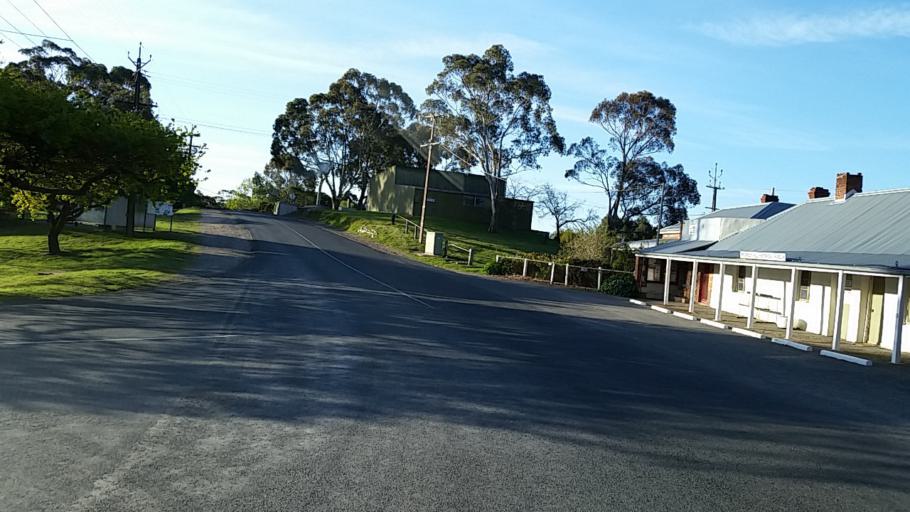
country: AU
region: South Australia
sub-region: Mount Barker
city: Meadows
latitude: -35.2244
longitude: 138.7341
